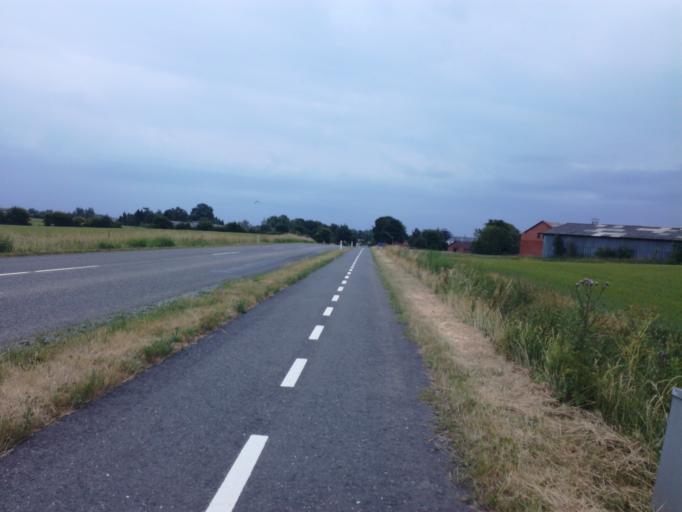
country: DK
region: South Denmark
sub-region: Vejle Kommune
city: Borkop
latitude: 55.6704
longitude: 9.6198
